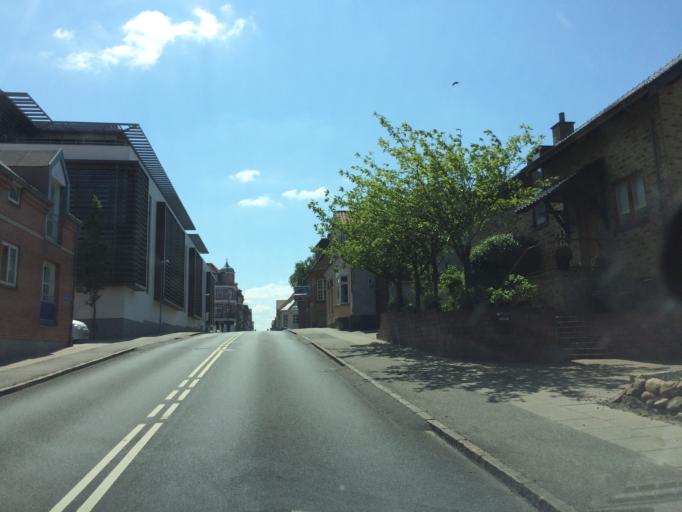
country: DK
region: Central Jutland
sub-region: Silkeborg Kommune
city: Silkeborg
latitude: 56.1690
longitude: 9.5435
